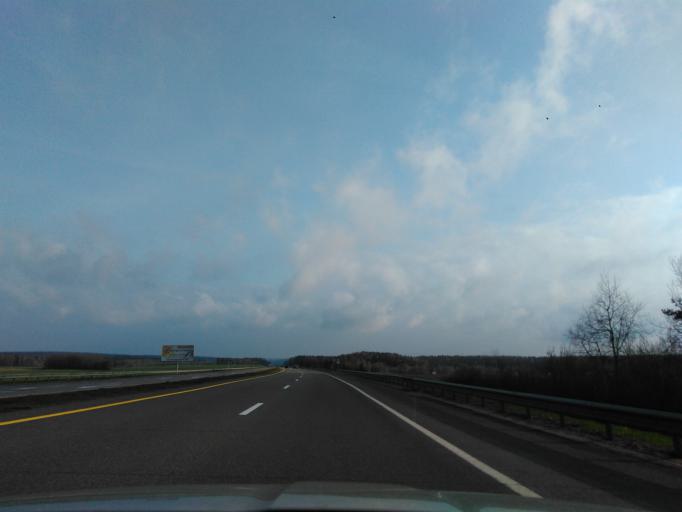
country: BY
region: Minsk
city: Lahoysk
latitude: 54.1532
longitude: 27.8105
